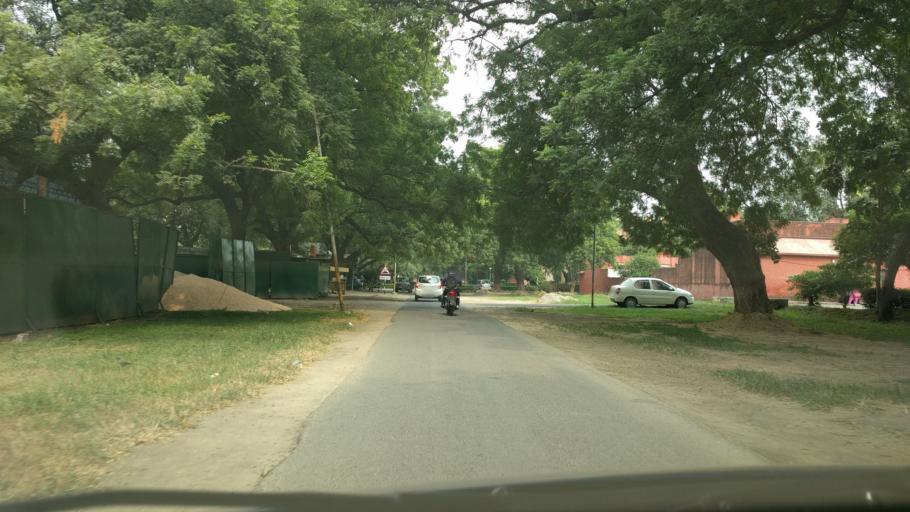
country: IN
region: NCT
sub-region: Central Delhi
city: Karol Bagh
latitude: 28.6357
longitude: 77.1631
